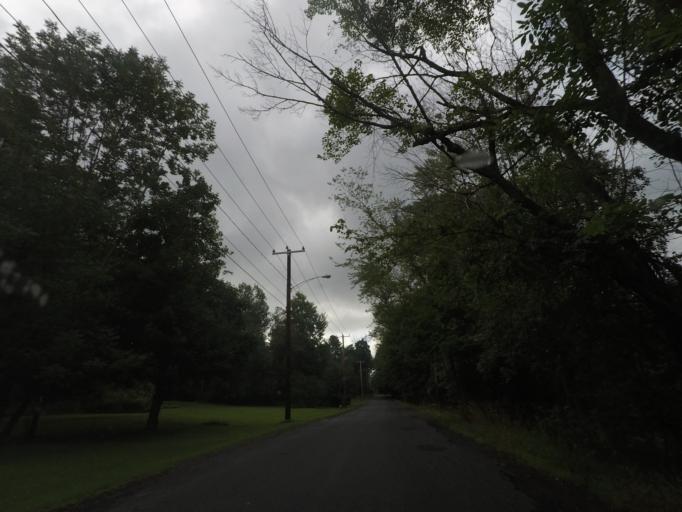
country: US
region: Massachusetts
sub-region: Berkshire County
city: Richmond
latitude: 42.4287
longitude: -73.3191
